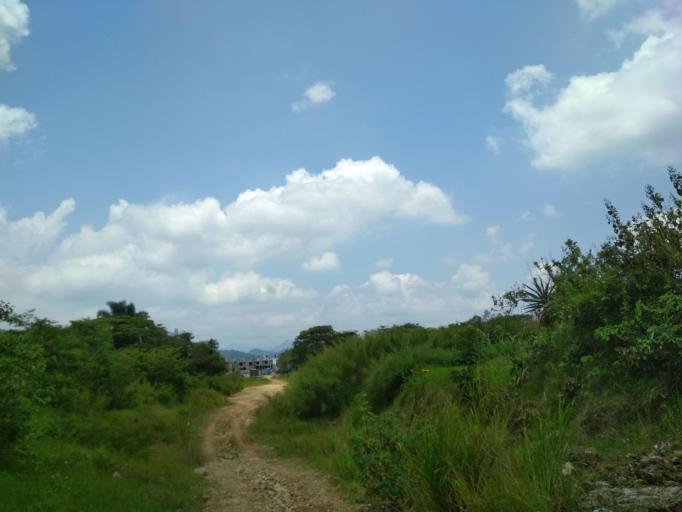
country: MX
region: Veracruz
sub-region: Ixtaczoquitlan
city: Buenavista
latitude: 18.8853
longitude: -97.0621
